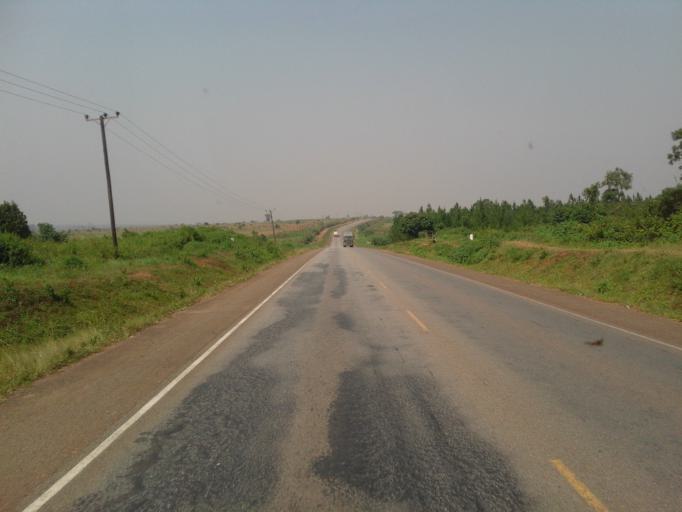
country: UG
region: Eastern Region
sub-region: Iganga District
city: Iganga
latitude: 0.6304
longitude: 33.5405
